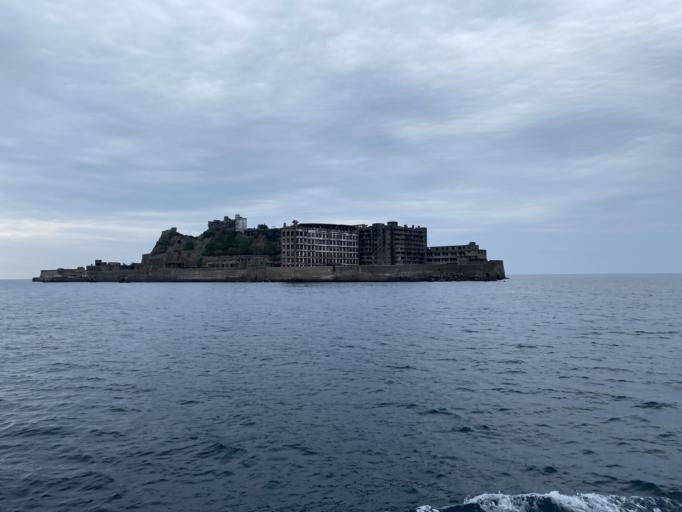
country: JP
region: Nagasaki
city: Nagasaki-shi
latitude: 32.6294
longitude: 129.7425
